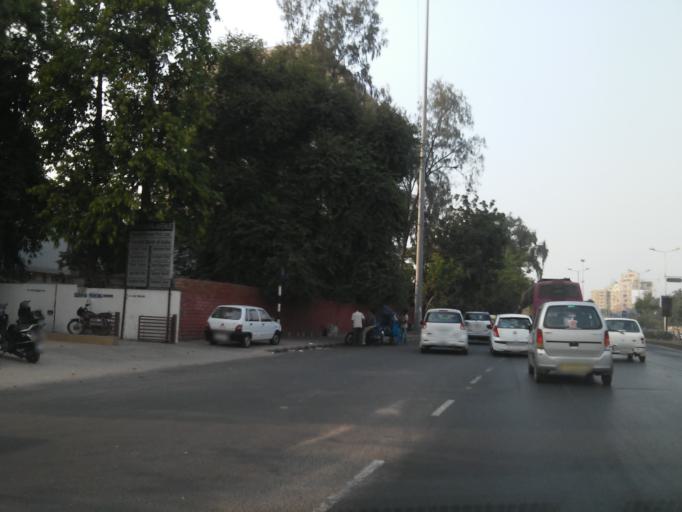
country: IN
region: Gujarat
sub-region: Ahmadabad
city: Ahmedabad
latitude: 23.0156
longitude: 72.5446
